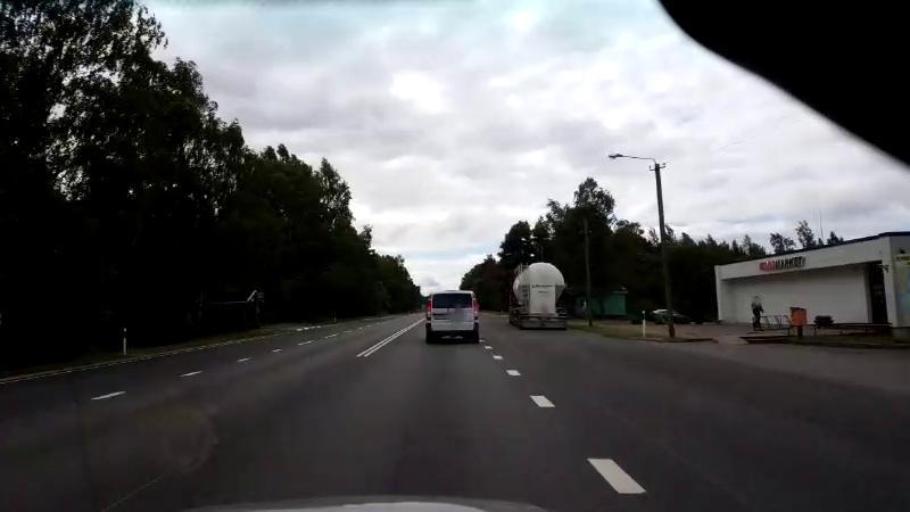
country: EE
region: Paernumaa
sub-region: Paernu linn
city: Parnu
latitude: 58.2034
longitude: 24.4854
